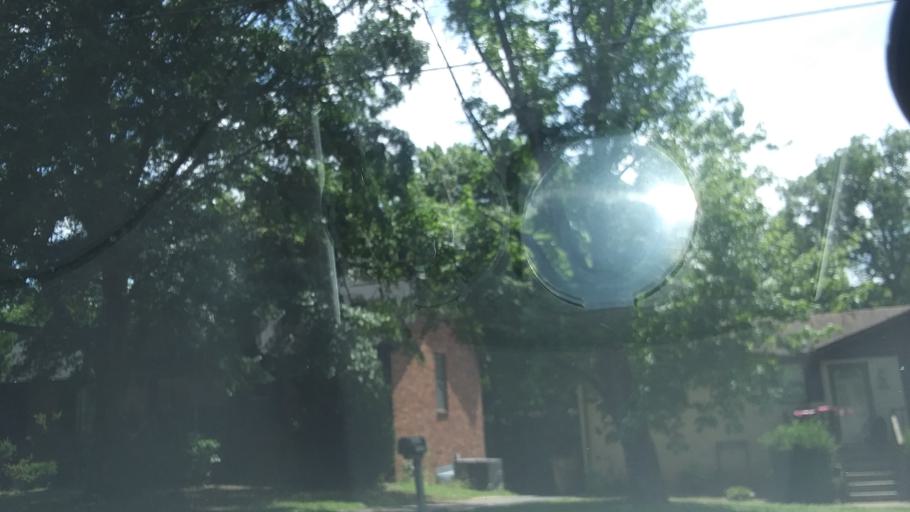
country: US
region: Tennessee
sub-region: Rutherford County
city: La Vergne
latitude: 36.0848
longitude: -86.6321
